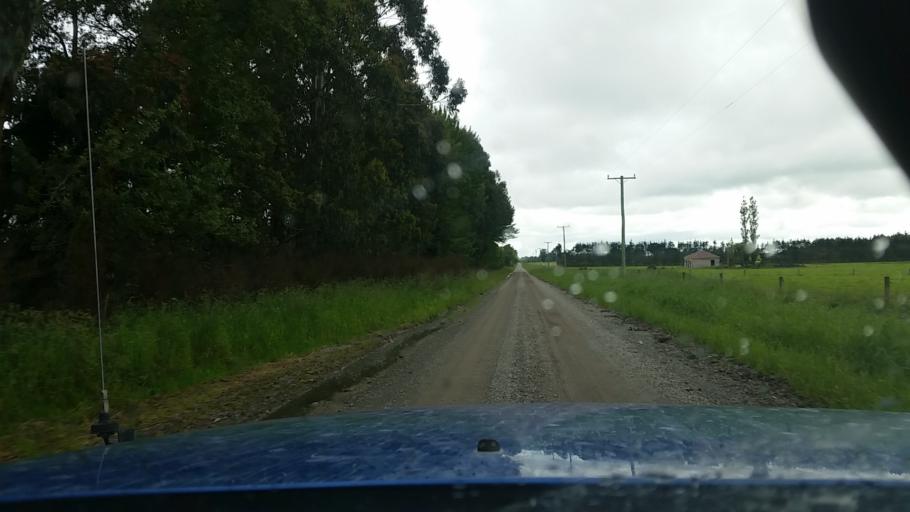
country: NZ
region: Canterbury
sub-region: Ashburton District
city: Methven
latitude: -43.6953
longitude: 171.4146
